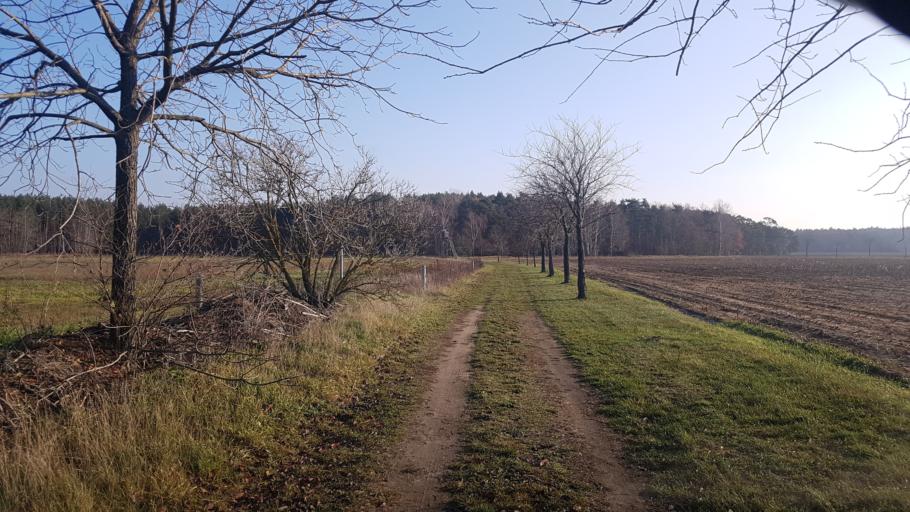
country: DE
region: Brandenburg
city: Tettau
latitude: 51.4346
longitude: 13.7378
